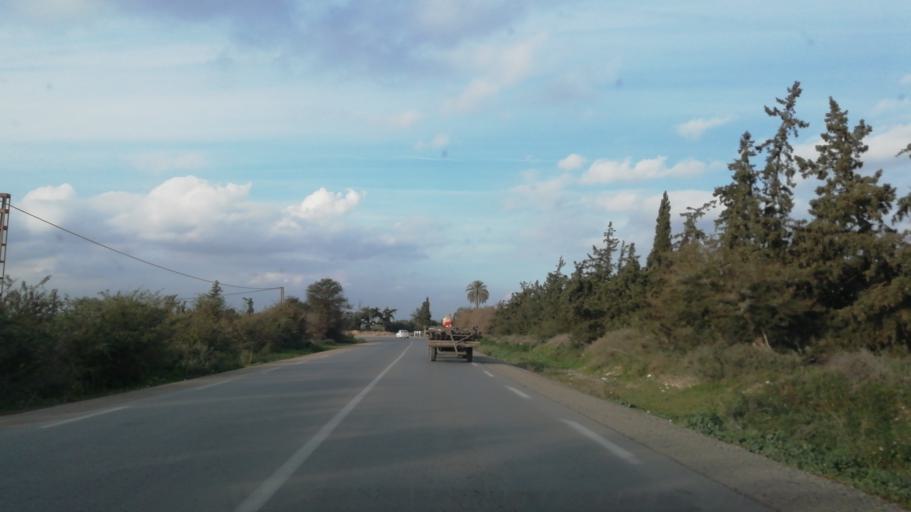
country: DZ
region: Mascara
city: Mascara
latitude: 35.6156
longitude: 0.0516
